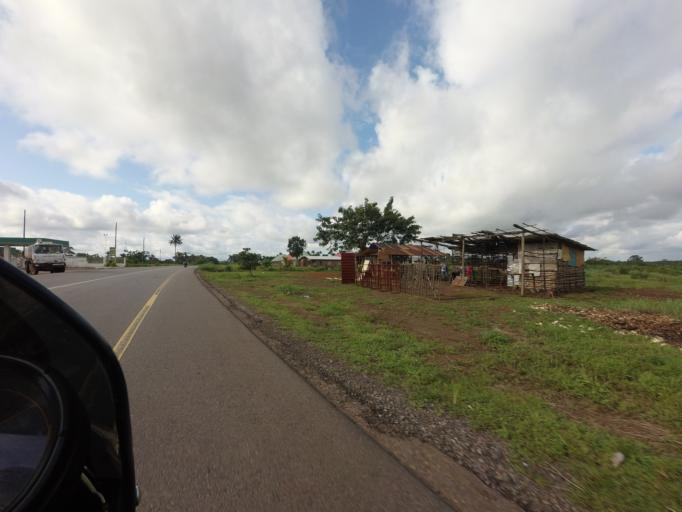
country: SL
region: Northern Province
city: Kambia
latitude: 9.0598
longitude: -12.9168
